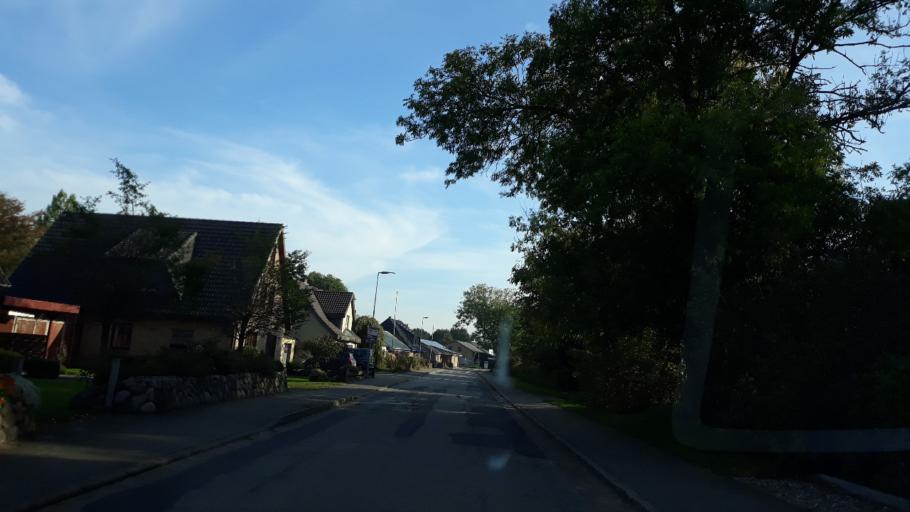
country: DE
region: Schleswig-Holstein
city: Borm
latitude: 54.4056
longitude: 9.3762
